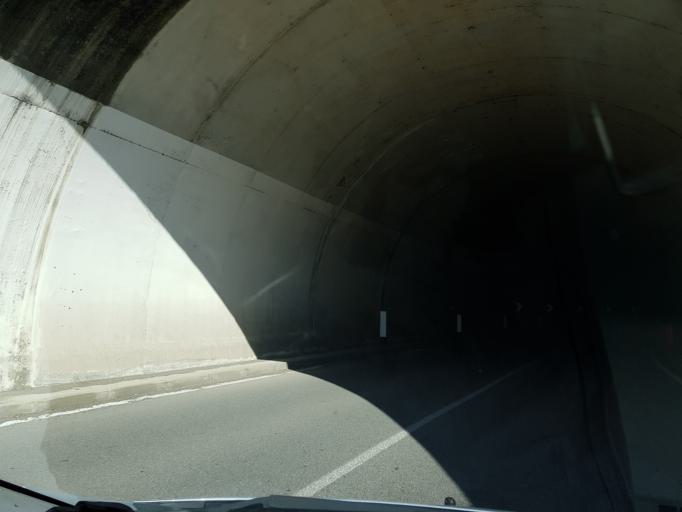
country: IT
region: Tuscany
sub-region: Provincia di Lucca
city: Piazza al Serchio-San Michele
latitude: 44.1808
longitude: 10.3093
